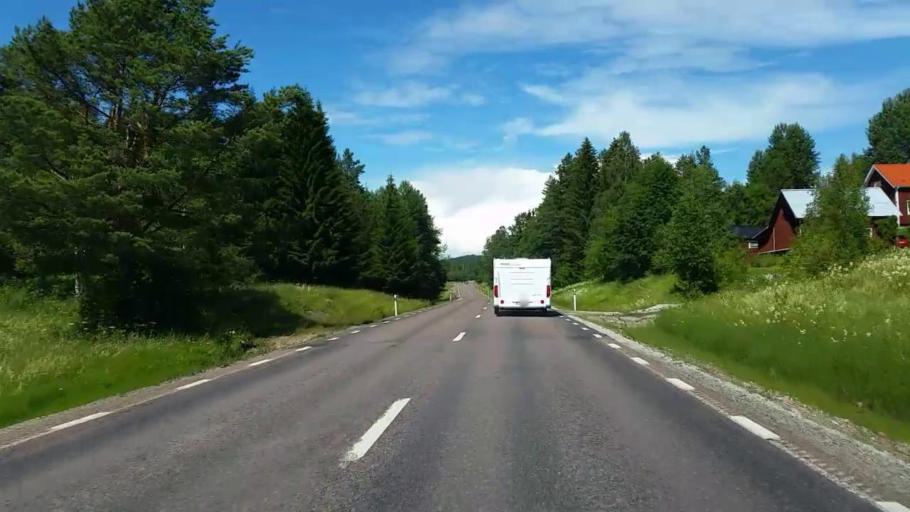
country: SE
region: Dalarna
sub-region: Rattviks Kommun
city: Raettvik
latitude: 60.9868
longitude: 15.2208
